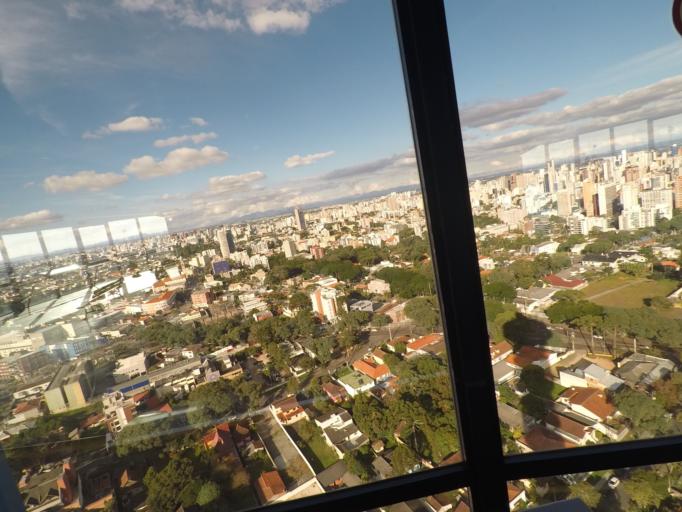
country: BR
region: Parana
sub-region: Curitiba
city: Curitiba
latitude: -25.4241
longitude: -49.2945
